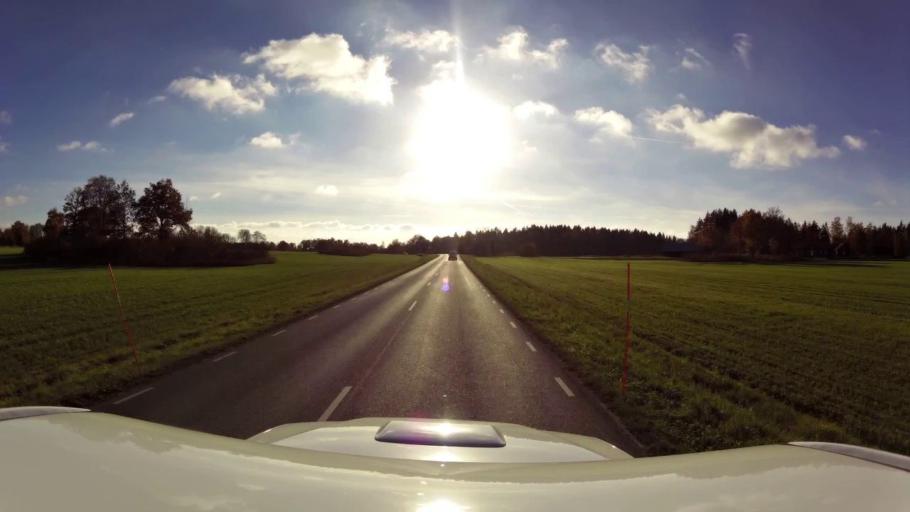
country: SE
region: OEstergoetland
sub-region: Linkopings Kommun
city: Malmslatt
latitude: 58.3383
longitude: 15.5139
